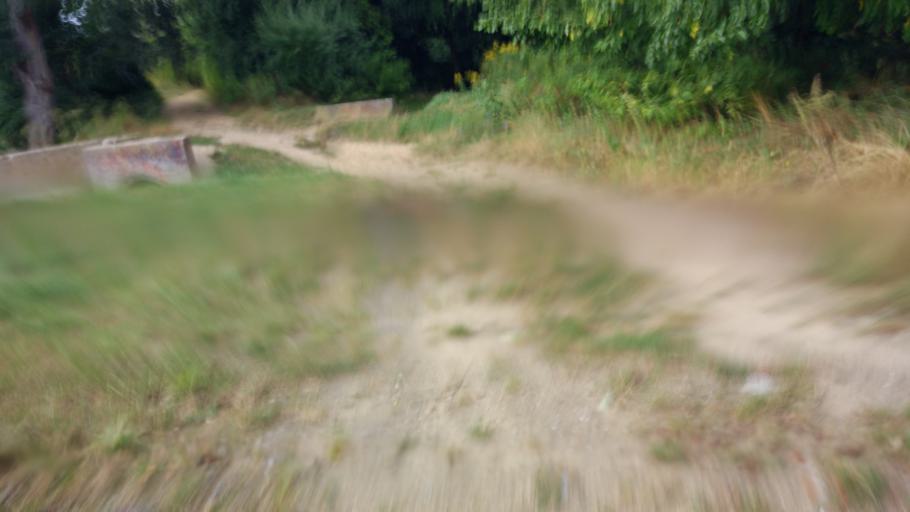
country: PL
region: Masovian Voivodeship
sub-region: Plock
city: Plock
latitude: 52.5254
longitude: 19.7495
